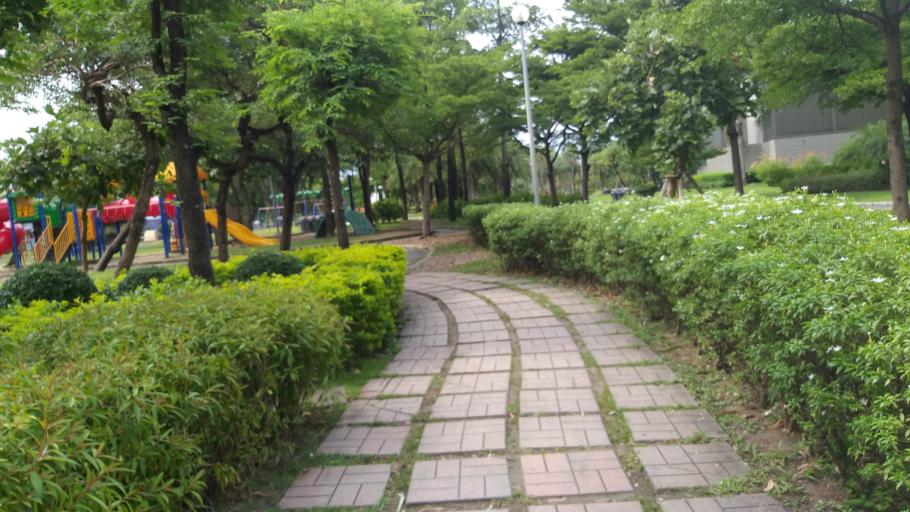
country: TH
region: Bangkok
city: Bang Sue
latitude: 13.8014
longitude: 100.5524
